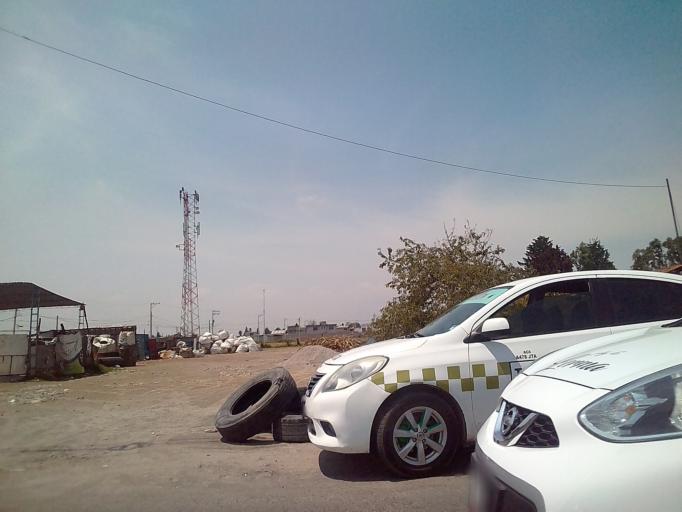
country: MX
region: Mexico
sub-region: Toluca
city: San Nicolas Tolentino
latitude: 19.3660
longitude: -99.5681
